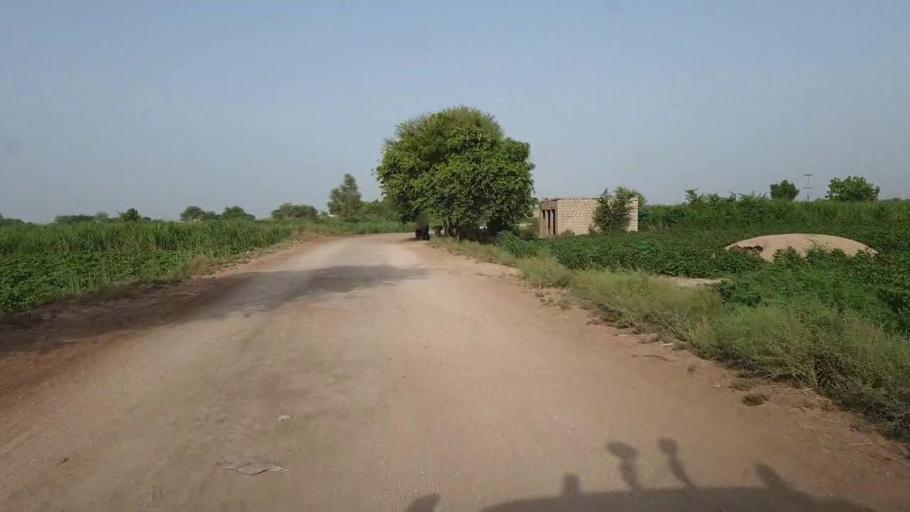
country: PK
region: Sindh
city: Daur
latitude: 26.3430
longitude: 68.2808
